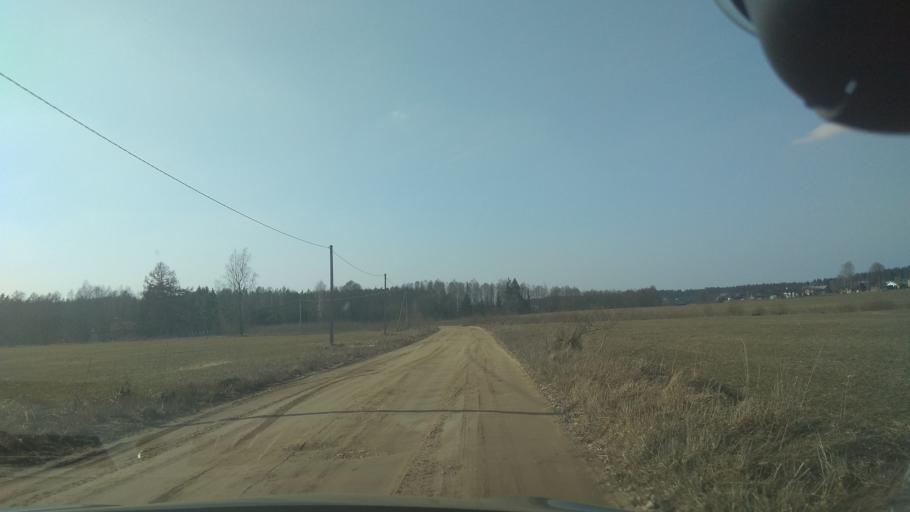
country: LT
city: Baltoji Voke
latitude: 54.4827
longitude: 25.2660
